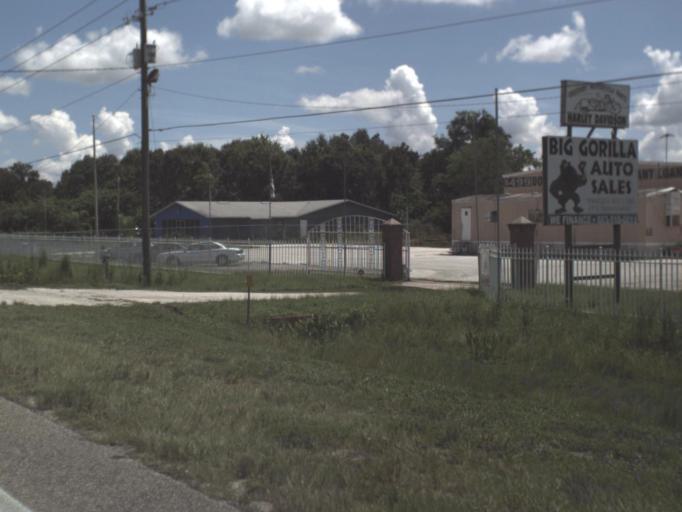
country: US
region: Florida
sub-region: Polk County
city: Combee Settlement
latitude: 28.0478
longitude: -81.8852
